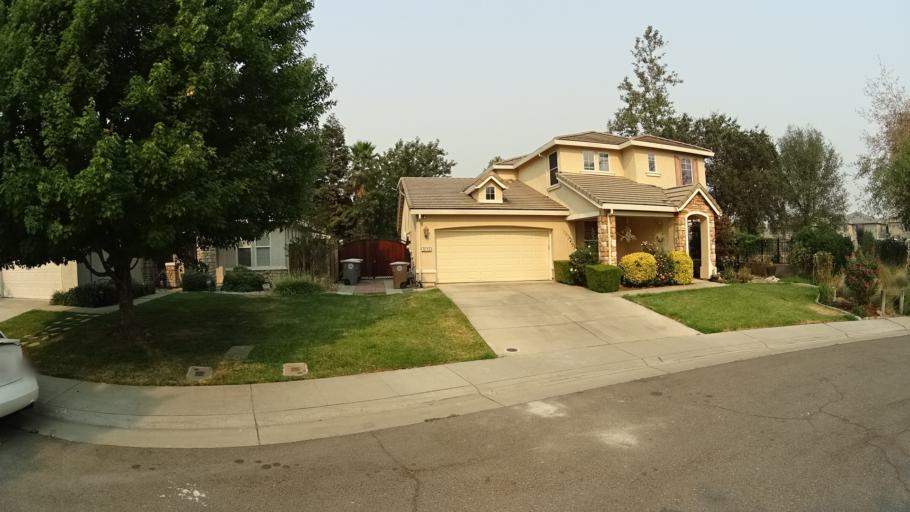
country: US
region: California
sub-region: Sacramento County
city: Laguna
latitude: 38.4048
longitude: -121.4466
